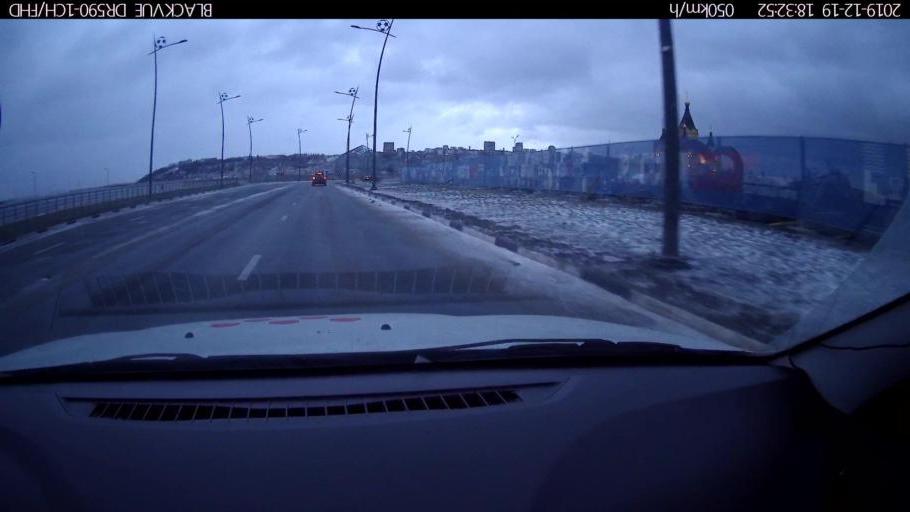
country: RU
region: Nizjnij Novgorod
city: Nizhniy Novgorod
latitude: 56.3368
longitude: 43.9709
